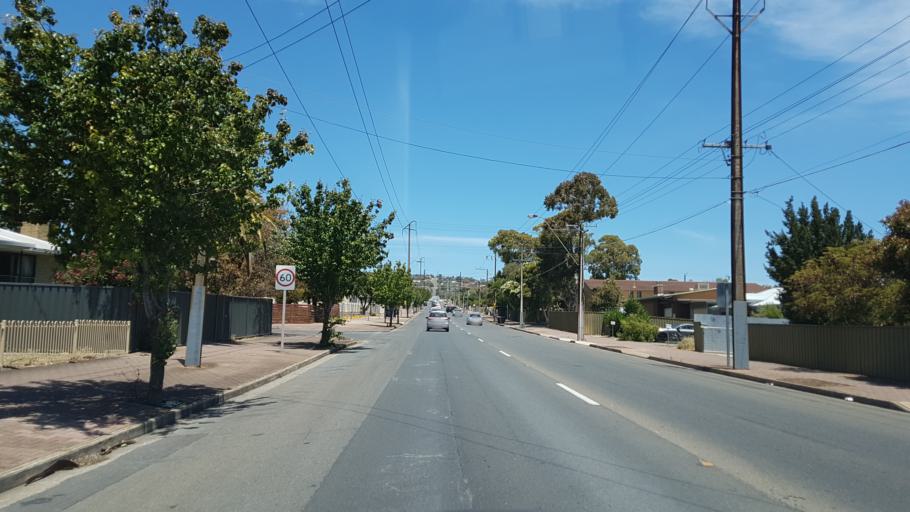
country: AU
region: South Australia
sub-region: Marion
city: Sturt
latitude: -35.0236
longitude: 138.5413
